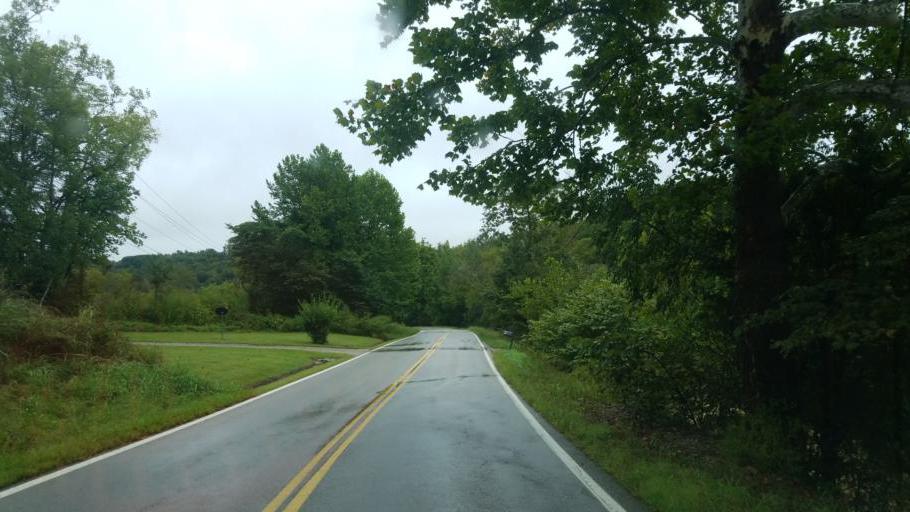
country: US
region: Ohio
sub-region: Adams County
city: West Union
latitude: 38.7534
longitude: -83.5185
